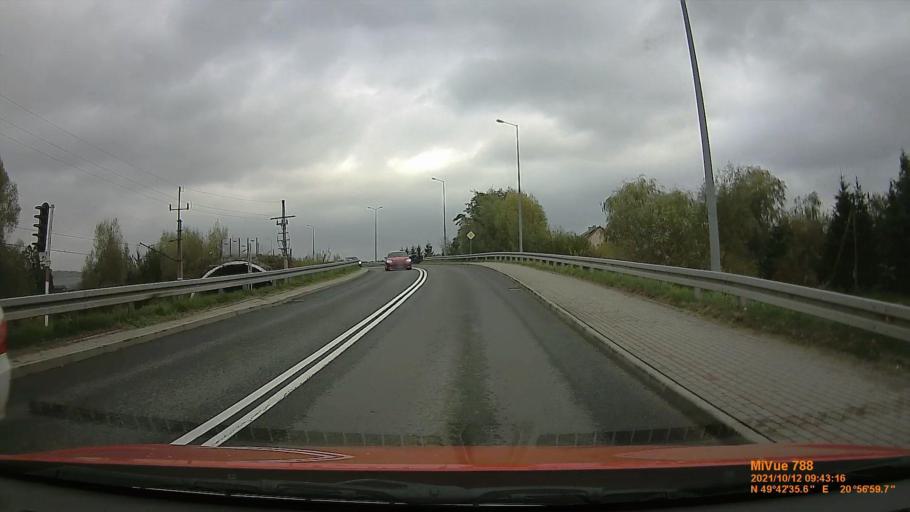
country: PL
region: Lesser Poland Voivodeship
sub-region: Powiat gorlicki
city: Bobowa
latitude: 49.7099
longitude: 20.9501
